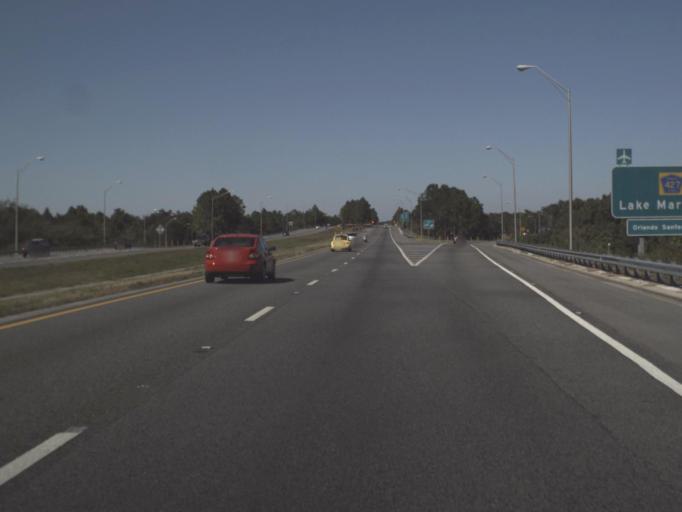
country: US
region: Florida
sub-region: Seminole County
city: Sanford
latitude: 28.7529
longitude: -81.2669
